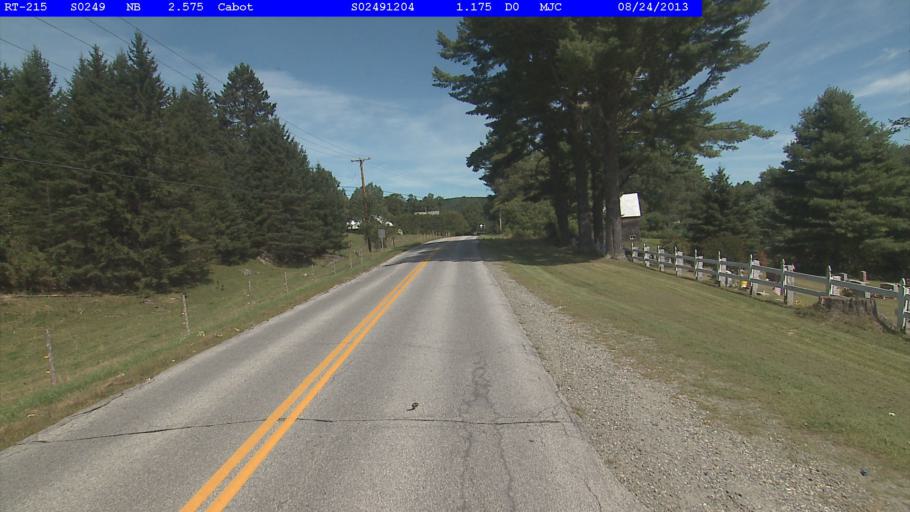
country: US
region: Vermont
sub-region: Caledonia County
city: Hardwick
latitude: 44.3840
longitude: -72.3340
